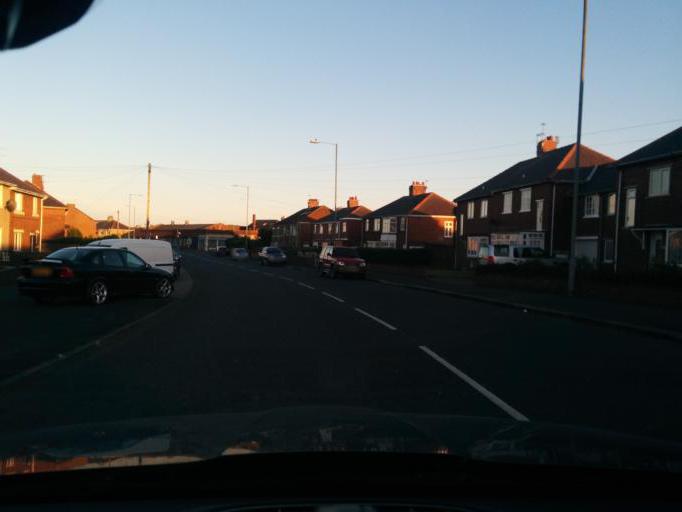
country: GB
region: England
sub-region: Northumberland
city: Newbiggin-by-the-Sea
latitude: 55.1889
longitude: -1.5217
